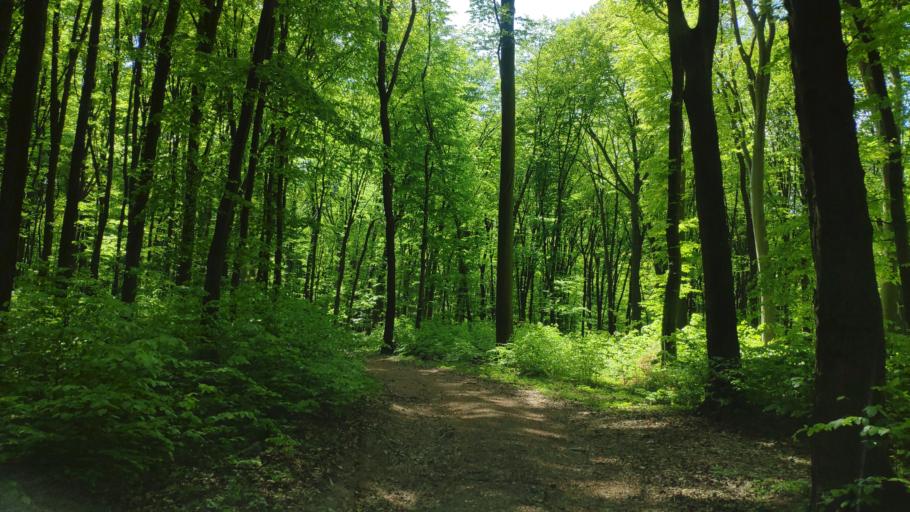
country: SK
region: Kosicky
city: Kosice
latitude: 48.6709
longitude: 21.4341
